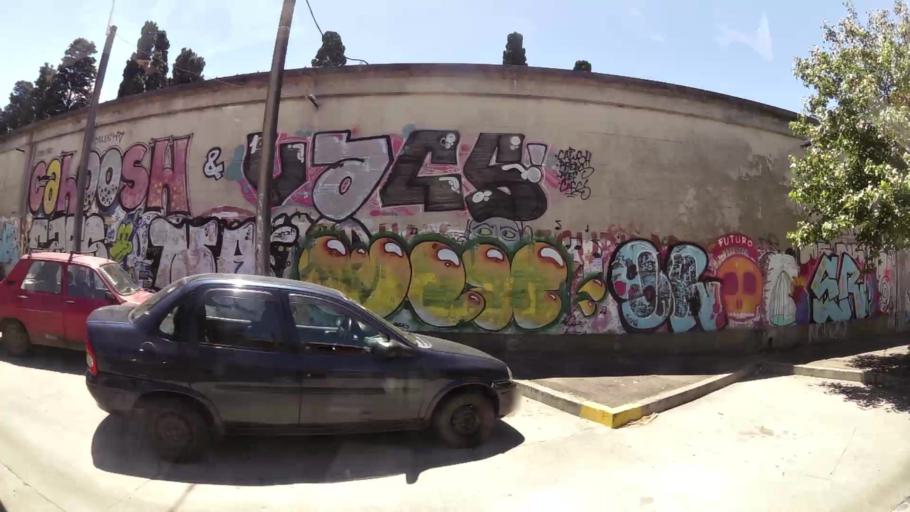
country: UY
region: Montevideo
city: Montevideo
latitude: -34.9018
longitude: -56.1273
